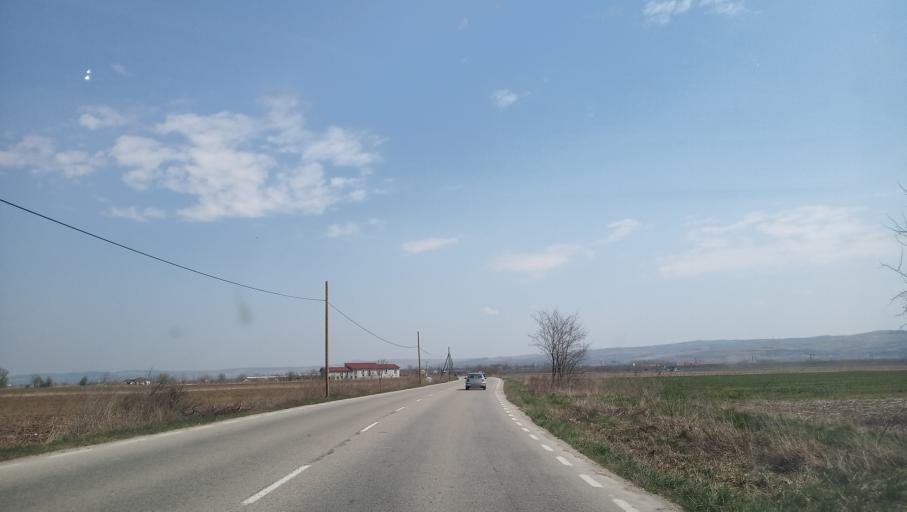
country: RO
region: Alba
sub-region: Municipiul Sebes
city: Lancram
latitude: 46.0227
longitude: 23.5291
